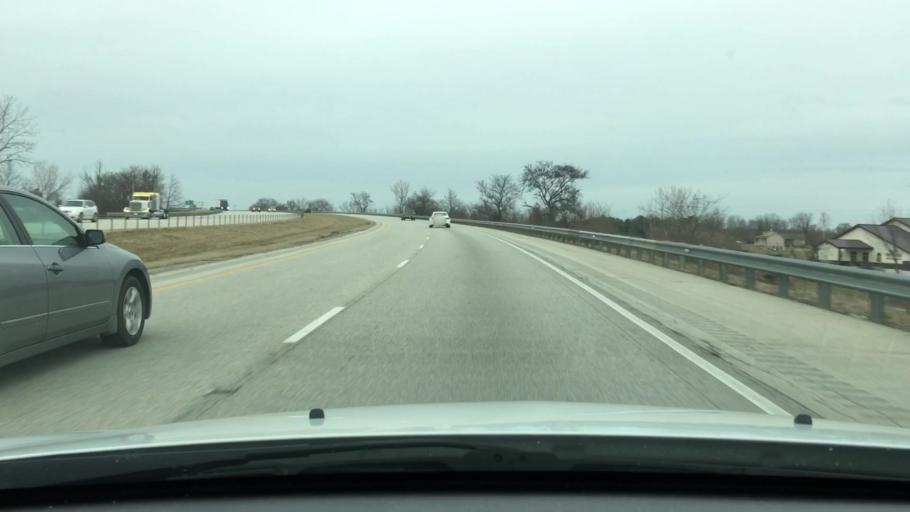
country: US
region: Illinois
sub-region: Sangamon County
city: Sherman
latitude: 39.8987
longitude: -89.5940
